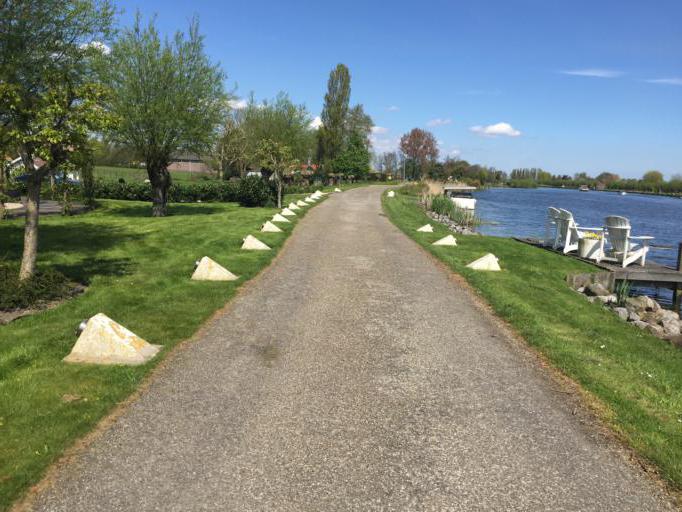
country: NL
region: North Holland
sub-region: Gemeente Aalsmeer
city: Aalsmeer
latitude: 52.2103
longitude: 4.7380
